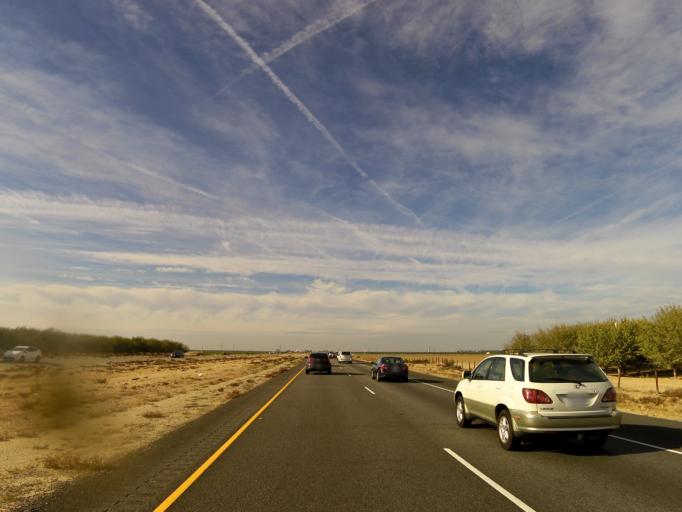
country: US
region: California
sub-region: Kern County
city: Buttonwillow
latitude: 35.4268
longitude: -119.4352
